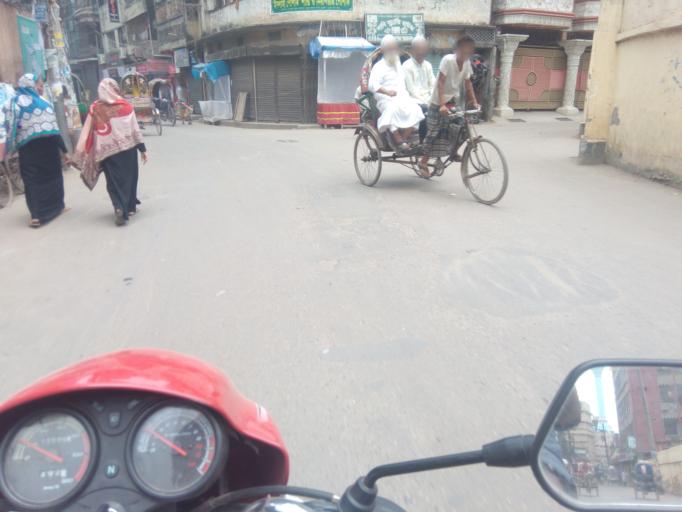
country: BD
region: Dhaka
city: Azimpur
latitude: 23.7188
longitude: 90.3900
